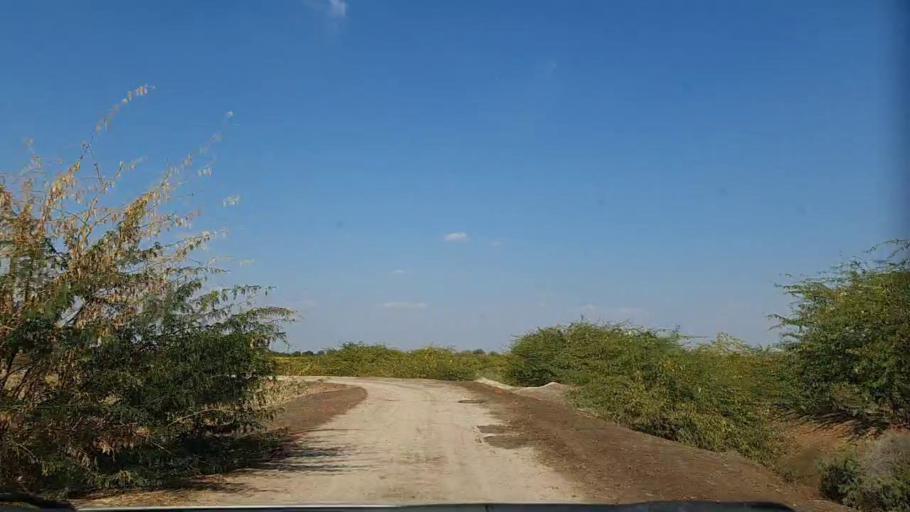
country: PK
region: Sindh
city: Pithoro
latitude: 25.6167
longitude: 69.3969
